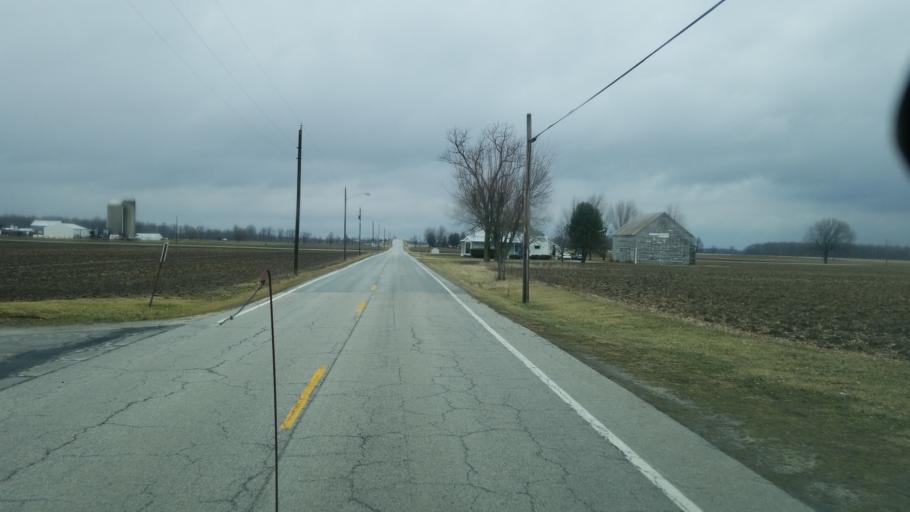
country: US
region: Ohio
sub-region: Hardin County
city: Forest
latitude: 40.8154
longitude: -83.4191
